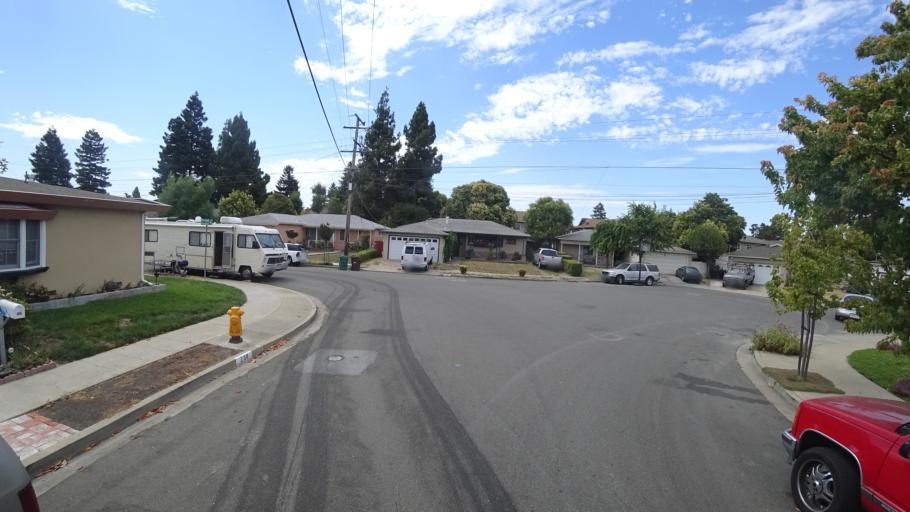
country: US
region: California
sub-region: Alameda County
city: Hayward
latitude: 37.6430
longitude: -122.0780
